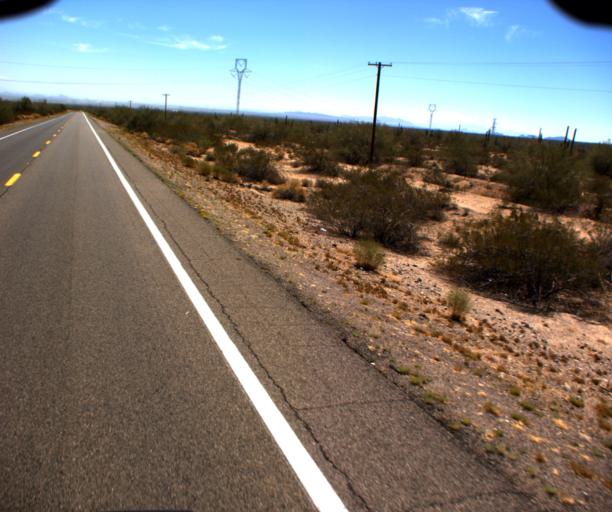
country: US
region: Arizona
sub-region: Pinal County
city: Maricopa
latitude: 32.8408
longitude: -112.1120
